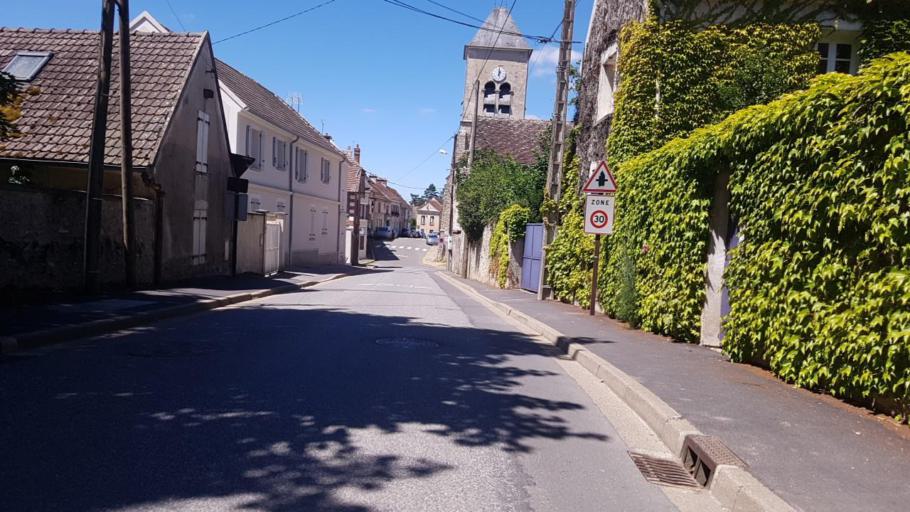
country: FR
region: Ile-de-France
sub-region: Departement de Seine-et-Marne
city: Sammeron
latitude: 48.9540
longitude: 3.0731
